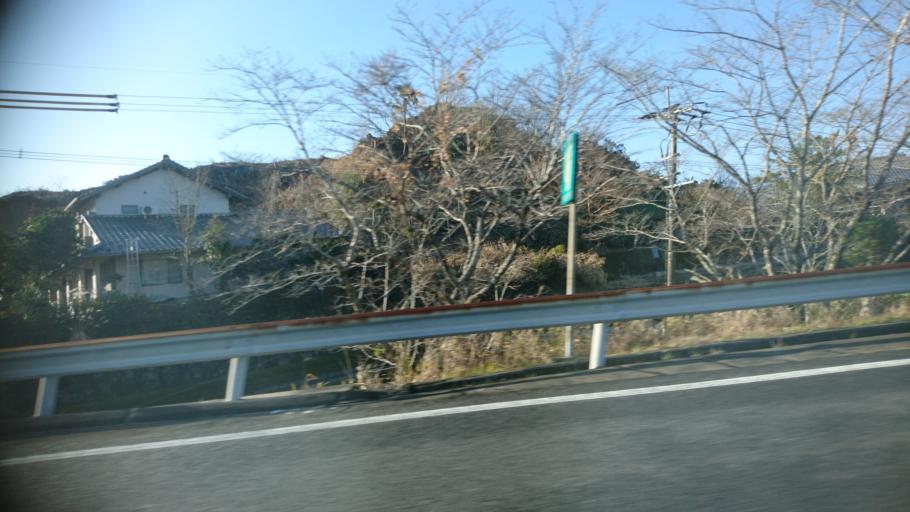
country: JP
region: Miyazaki
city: Kobayashi
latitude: 32.0340
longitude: 130.8096
